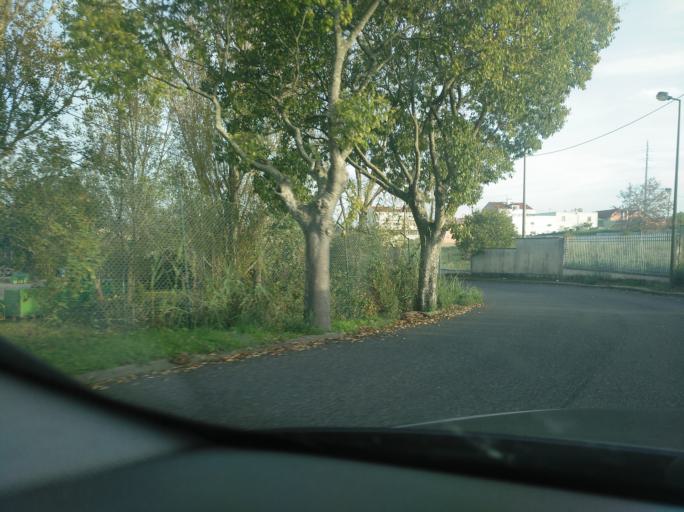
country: PT
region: Lisbon
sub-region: Odivelas
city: Odivelas
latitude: 38.7756
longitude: -9.1814
